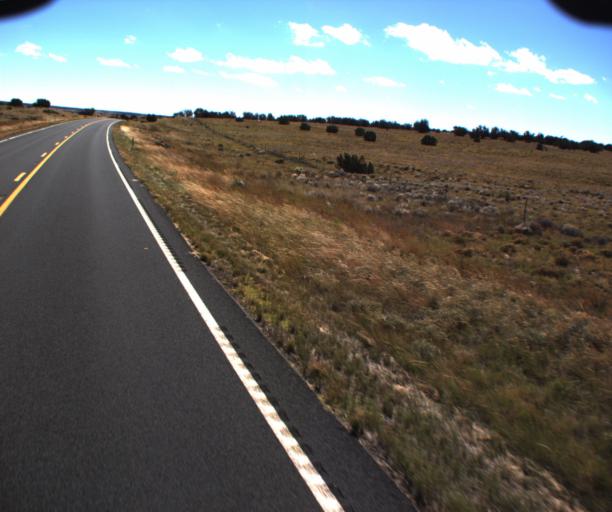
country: US
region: Arizona
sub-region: Apache County
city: Houck
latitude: 35.0281
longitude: -109.2493
